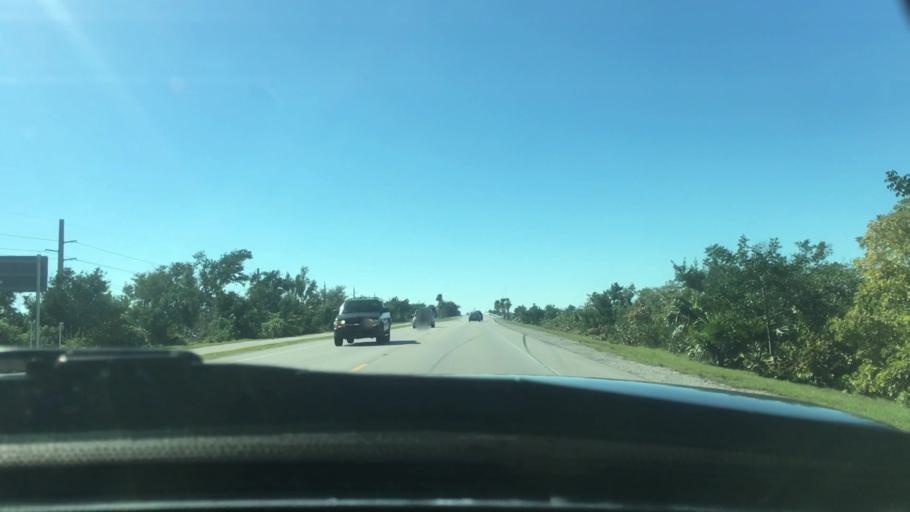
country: US
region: Florida
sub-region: Monroe County
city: Big Pine Key
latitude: 24.6681
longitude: -81.3796
